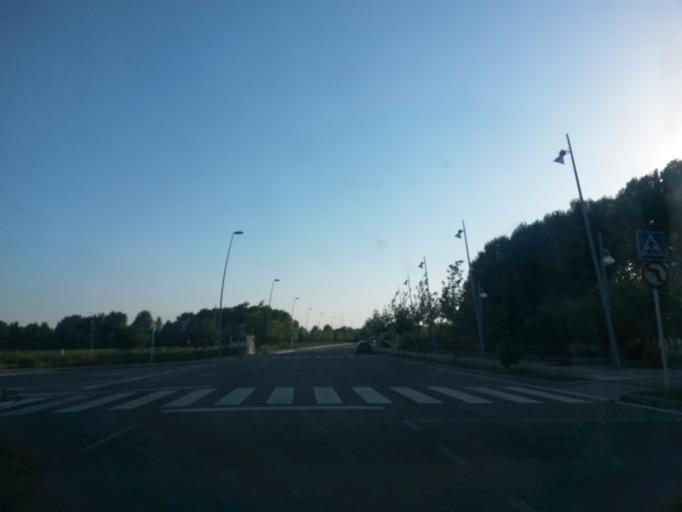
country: ES
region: Catalonia
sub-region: Provincia de Girona
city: Fornells de la Selva
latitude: 41.9464
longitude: 2.7969
